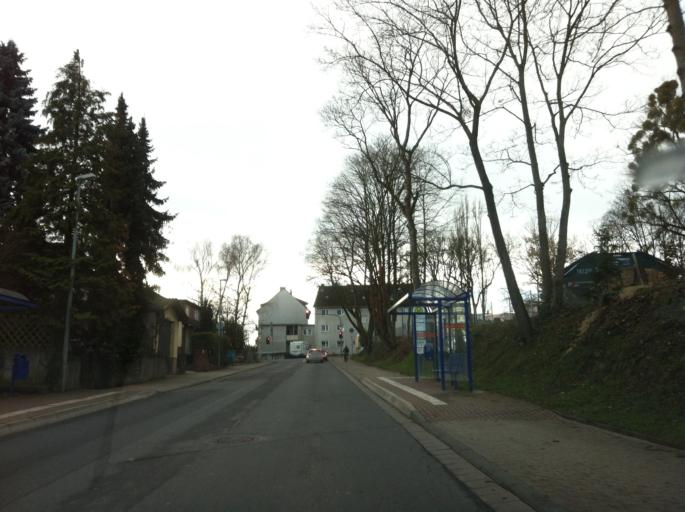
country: DE
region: Hesse
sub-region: Regierungsbezirk Darmstadt
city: Kronberg
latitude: 50.1765
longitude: 8.5221
